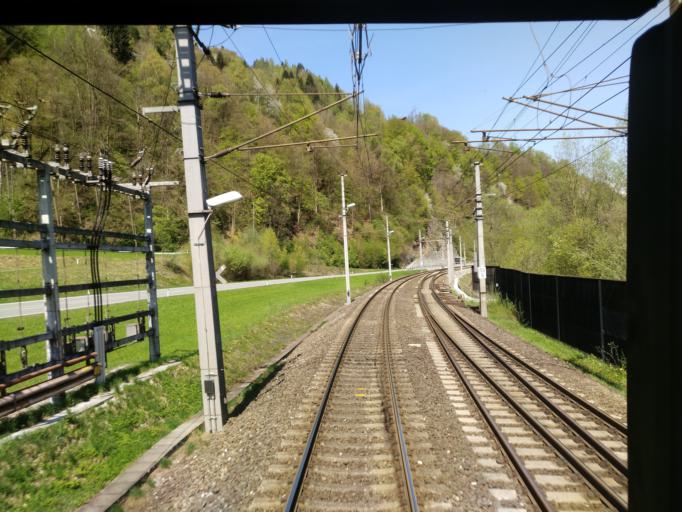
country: AT
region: Salzburg
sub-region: Politischer Bezirk Sankt Johann im Pongau
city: Bischofshofen
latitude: 47.3840
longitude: 13.2107
